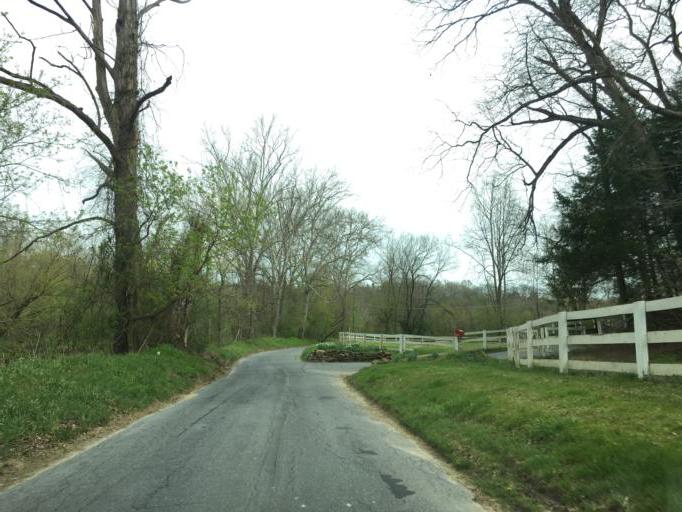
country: US
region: Maryland
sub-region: Baltimore County
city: Hunt Valley
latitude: 39.5522
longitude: -76.6380
